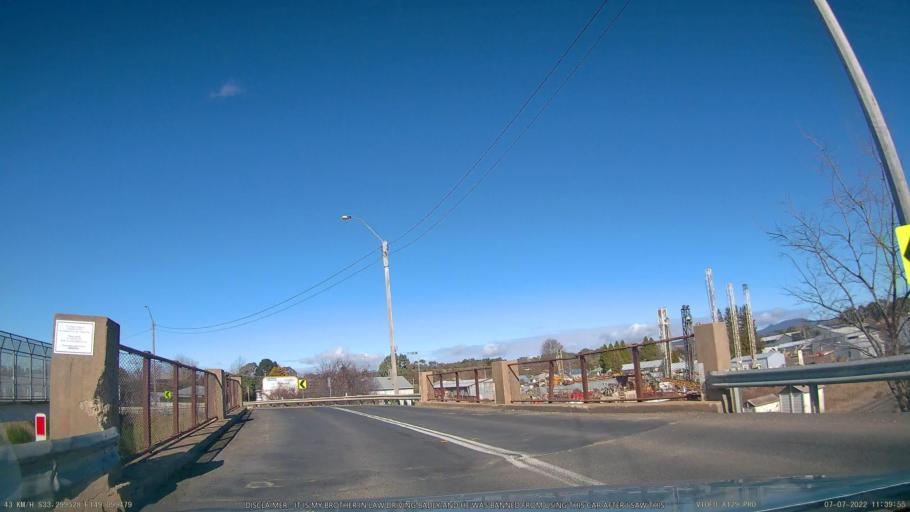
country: AU
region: New South Wales
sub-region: Orange Municipality
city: Orange
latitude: -33.2997
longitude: 149.0993
